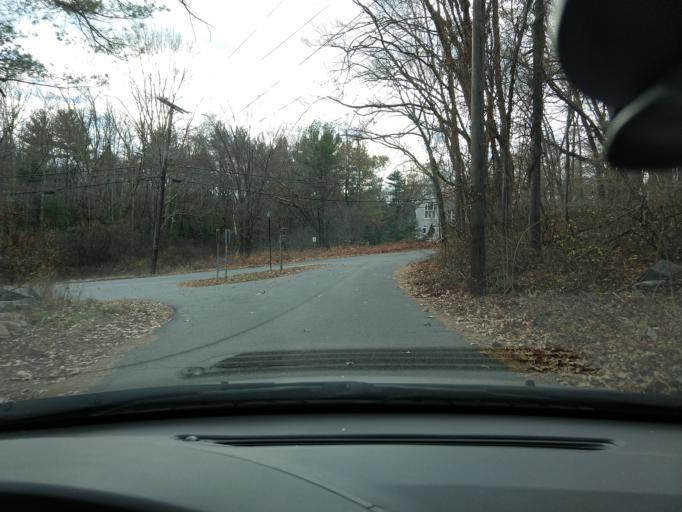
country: US
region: Massachusetts
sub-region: Middlesex County
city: Wayland
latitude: 42.3973
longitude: -71.3762
